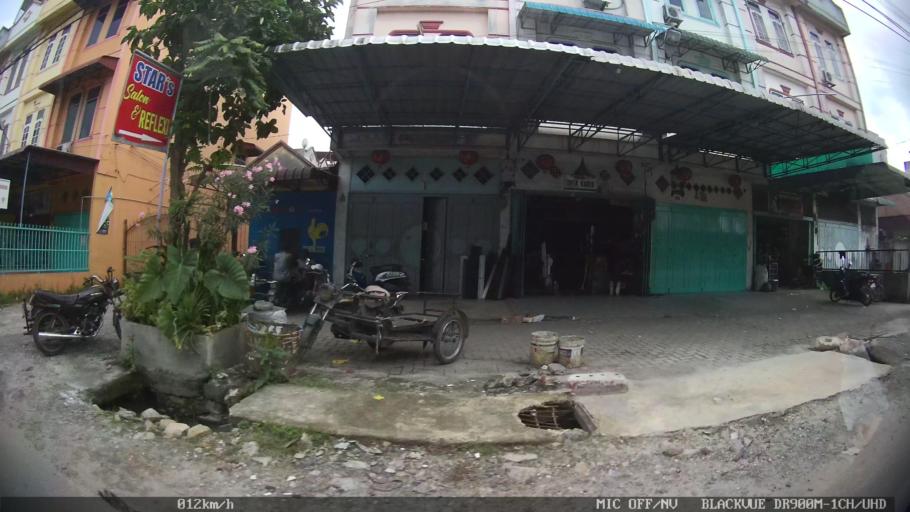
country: ID
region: North Sumatra
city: Percut
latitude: 3.5667
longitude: 98.8760
